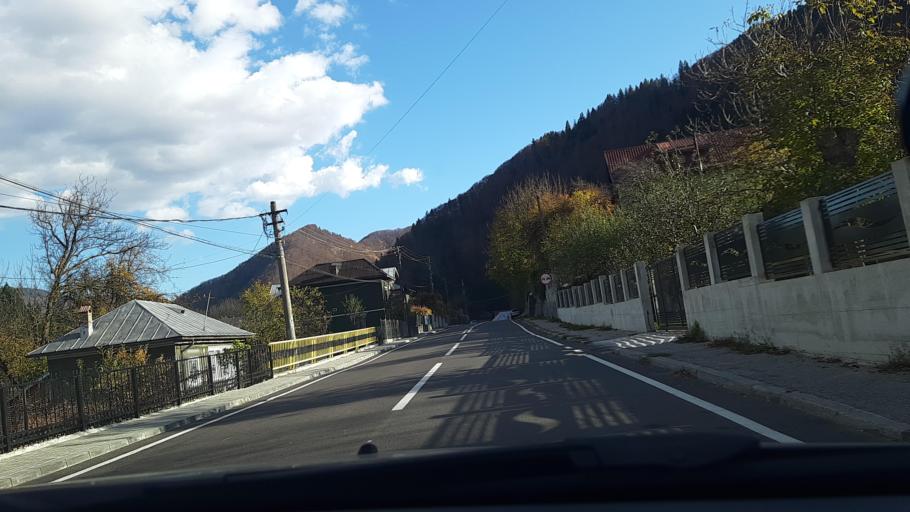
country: RO
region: Valcea
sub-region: Comuna Voineasa
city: Voineasa
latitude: 45.4136
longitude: 23.9622
